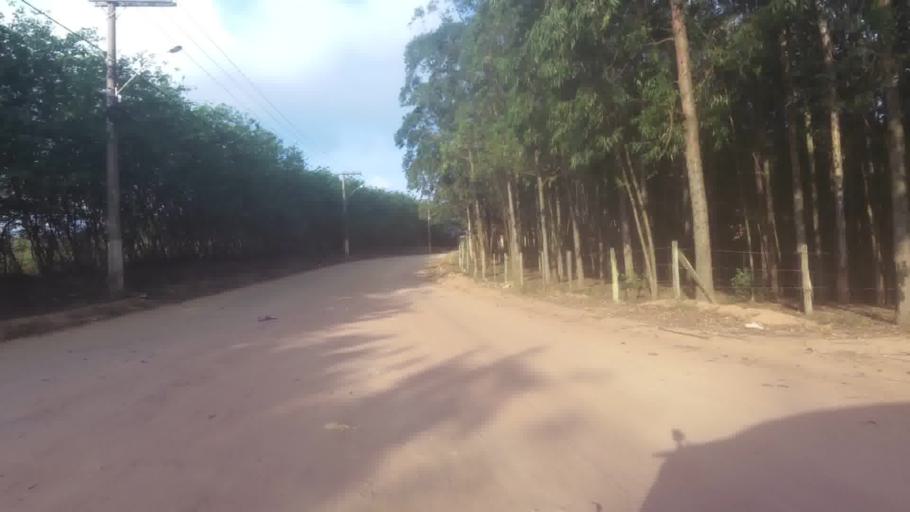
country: BR
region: Espirito Santo
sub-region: Itapemirim
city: Itapemirim
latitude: -21.0209
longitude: -40.8234
